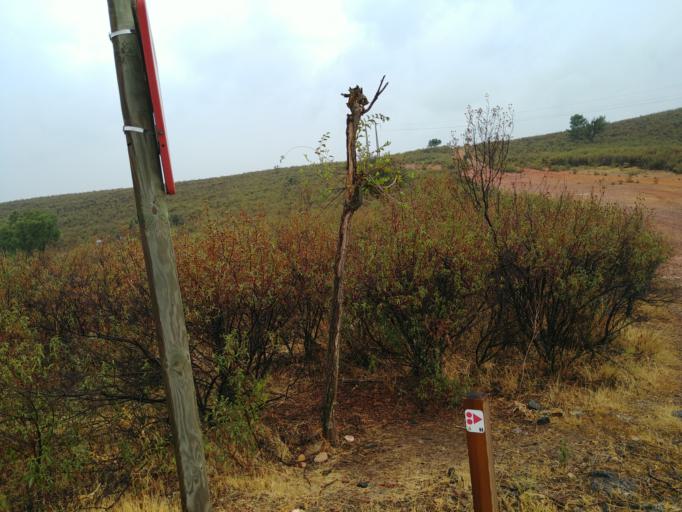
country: ES
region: Extremadura
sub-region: Provincia de Caceres
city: Torrejon el Rubio
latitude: 39.8554
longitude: -6.0270
